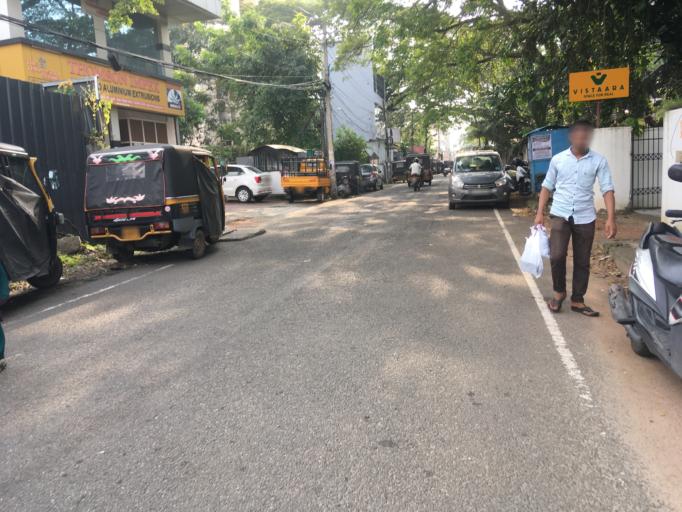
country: IN
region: Kerala
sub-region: Ernakulam
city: Cochin
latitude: 9.9742
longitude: 76.2820
